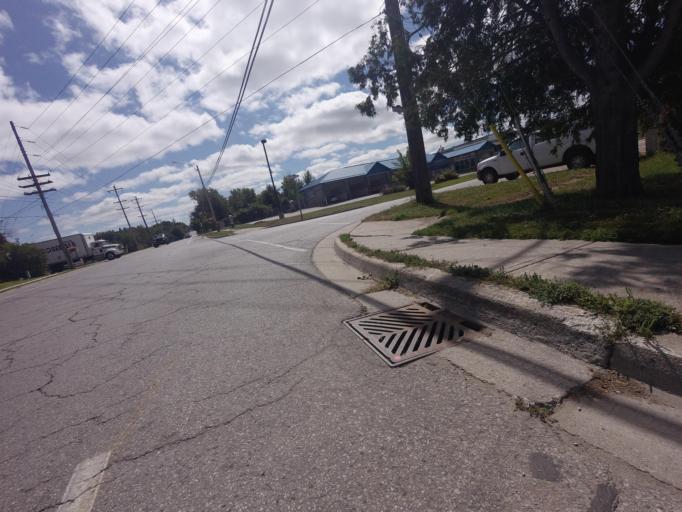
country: CA
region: Ontario
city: Uxbridge
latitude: 44.1147
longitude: -79.1229
